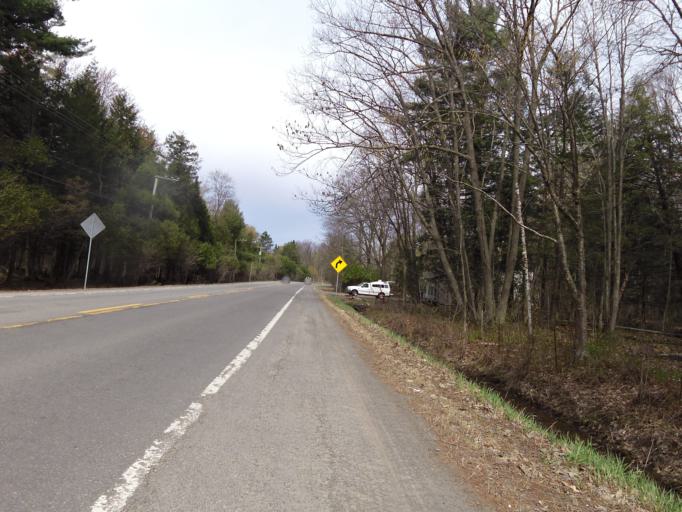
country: CA
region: Quebec
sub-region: Laurentides
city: Oka
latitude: 45.4667
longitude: -74.1115
